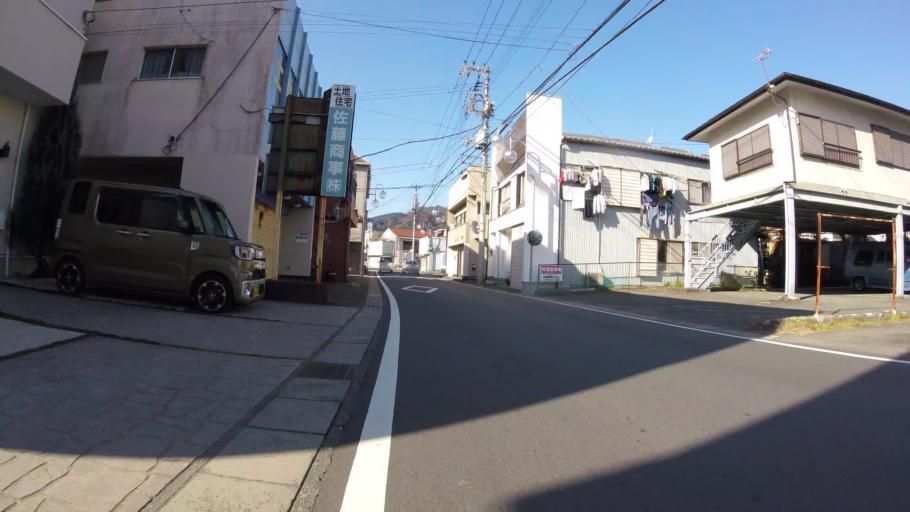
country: JP
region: Shizuoka
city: Mishima
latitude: 34.9929
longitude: 138.9404
